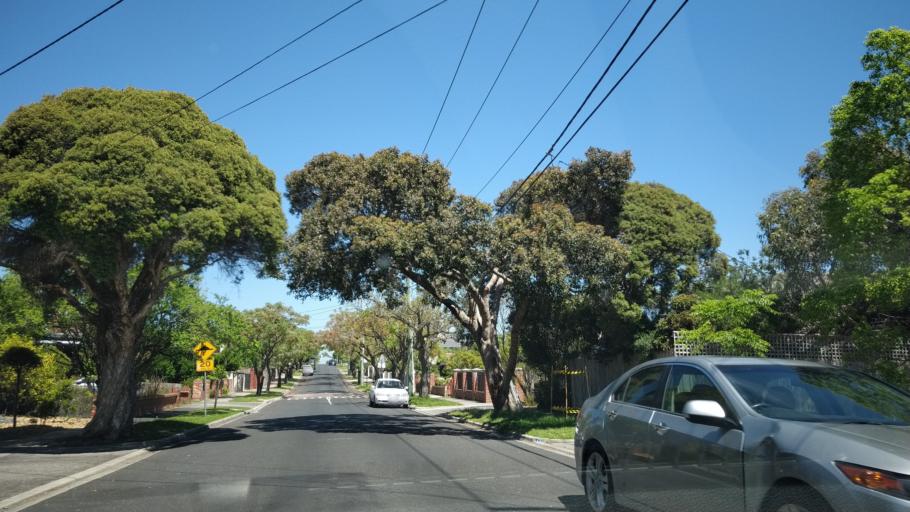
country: AU
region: Victoria
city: Ormond
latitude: -37.8999
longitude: 145.0309
